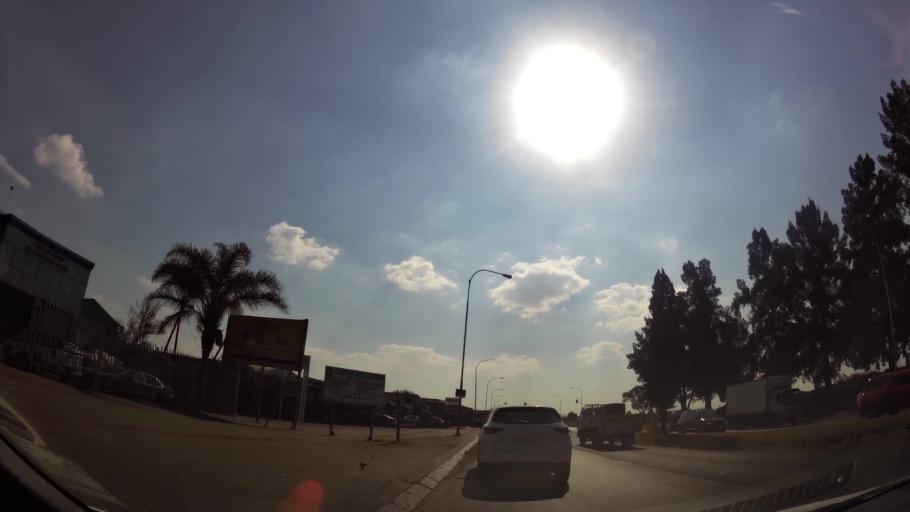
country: ZA
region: Gauteng
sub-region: Ekurhuleni Metropolitan Municipality
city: Boksburg
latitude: -26.2041
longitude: 28.2842
